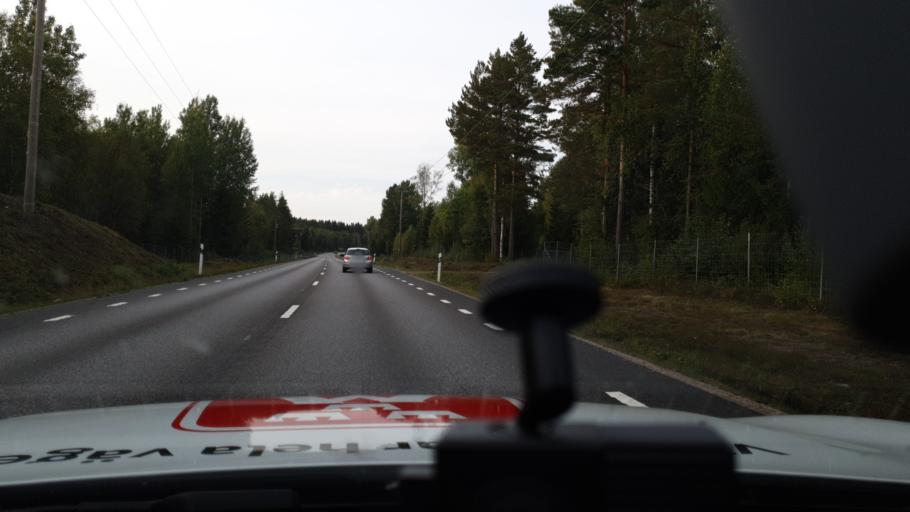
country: SE
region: Kronoberg
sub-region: Vaxjo Kommun
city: Braas
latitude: 57.2124
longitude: 15.1514
